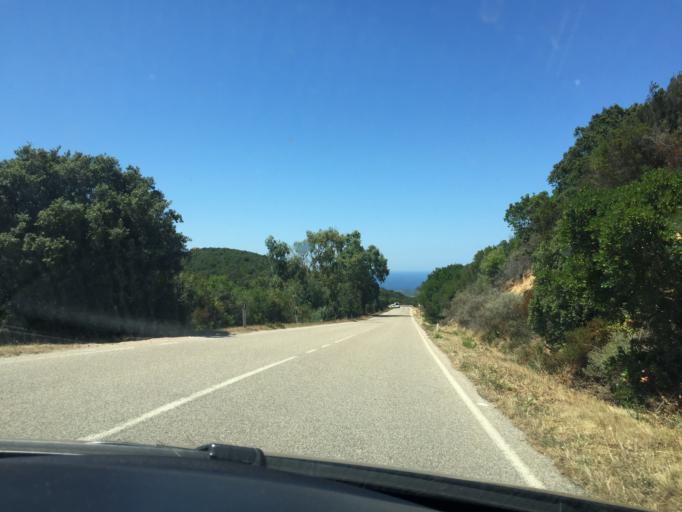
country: IT
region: Sardinia
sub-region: Provincia di Olbia-Tempio
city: Aglientu
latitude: 41.0876
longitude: 9.1078
